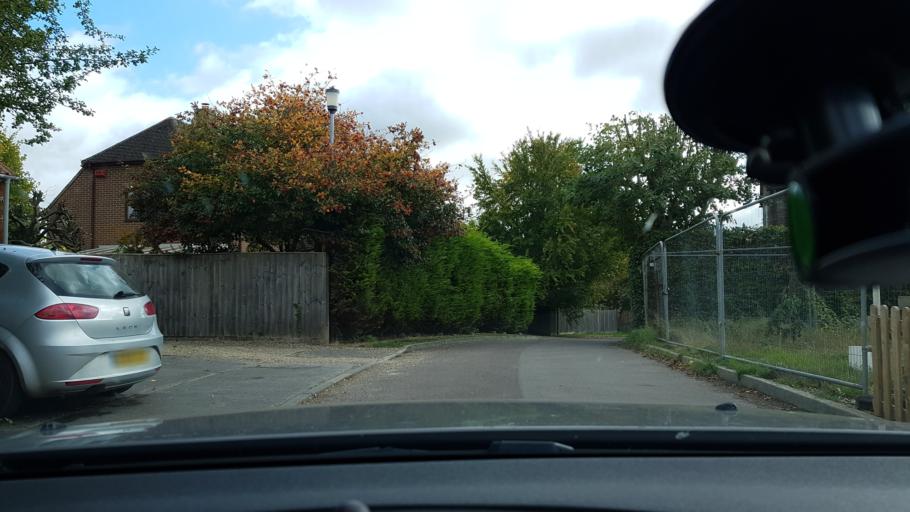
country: GB
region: England
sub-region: Wiltshire
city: Great Bedwyn
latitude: 51.3787
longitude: -1.6015
